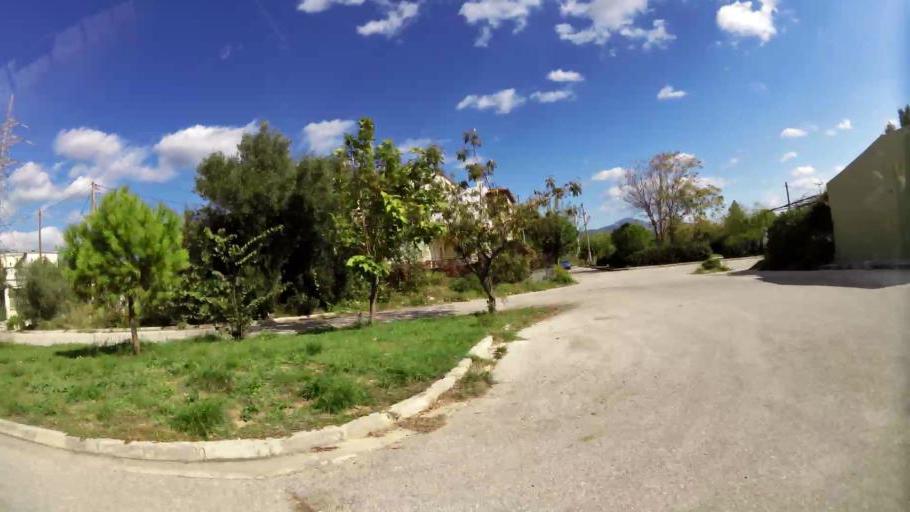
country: GR
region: Attica
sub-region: Nomarchia Anatolikis Attikis
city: Acharnes
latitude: 38.1006
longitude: 23.7378
